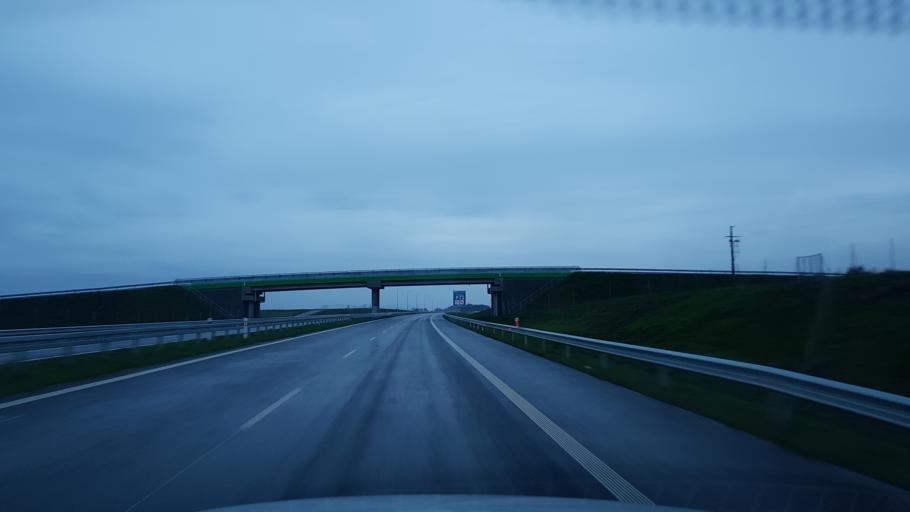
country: PL
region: West Pomeranian Voivodeship
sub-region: Powiat gryficki
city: Brojce
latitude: 53.9777
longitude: 15.4282
